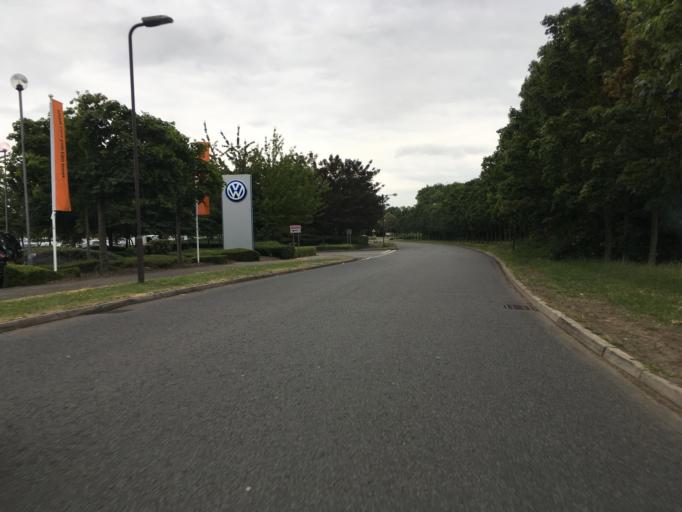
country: GB
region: England
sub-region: Milton Keynes
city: Broughton
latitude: 52.0381
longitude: -0.6911
